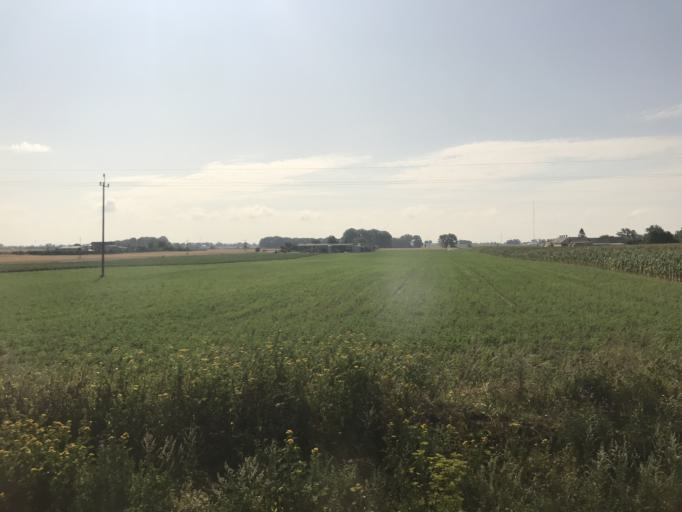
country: PL
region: Kujawsko-Pomorskie
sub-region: Powiat swiecki
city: Pruszcz
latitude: 53.3000
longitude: 18.1448
